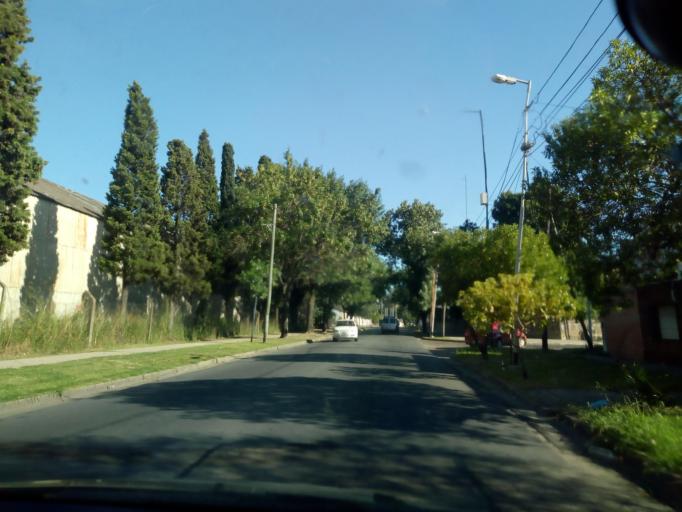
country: AR
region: Buenos Aires
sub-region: Partido de Avellaneda
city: Avellaneda
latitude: -34.6757
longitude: -58.3617
